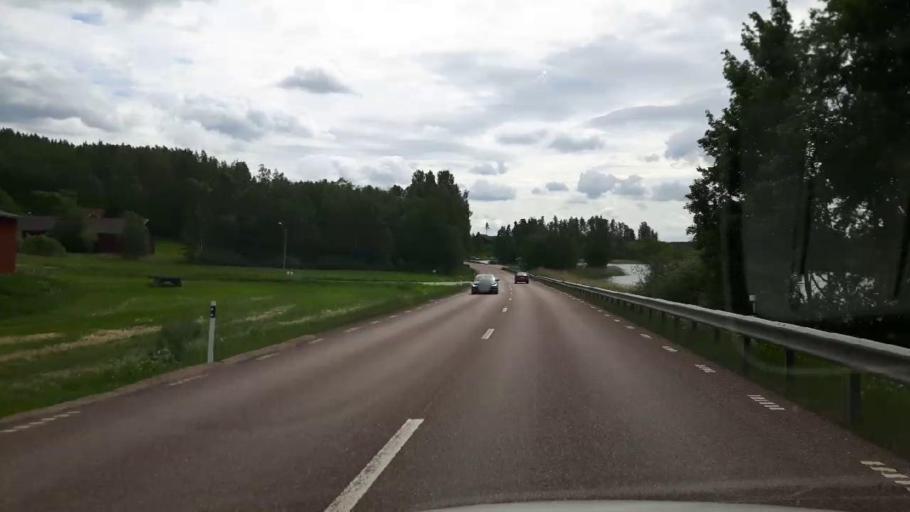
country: SE
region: Dalarna
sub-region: Hedemora Kommun
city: Hedemora
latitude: 60.3255
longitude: 15.9513
